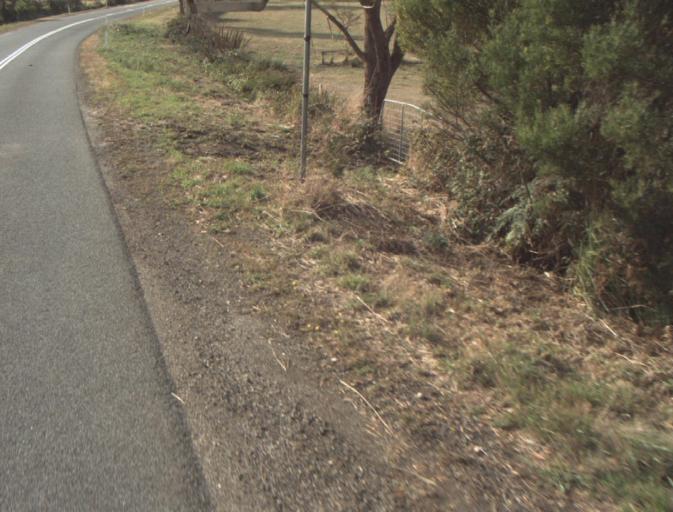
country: AU
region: Tasmania
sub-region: Launceston
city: Mayfield
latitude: -41.2245
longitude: 147.1223
